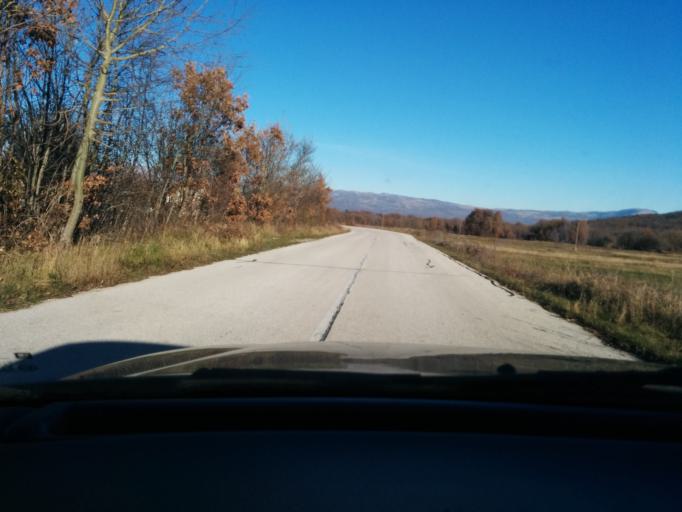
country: HR
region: Splitsko-Dalmatinska
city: Hrvace
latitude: 43.7440
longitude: 16.5446
